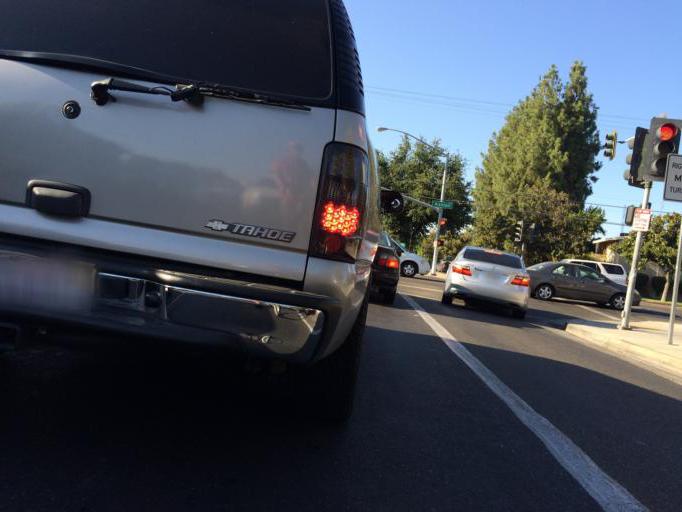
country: US
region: California
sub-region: Fresno County
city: Fresno
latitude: 36.7938
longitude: -119.7722
